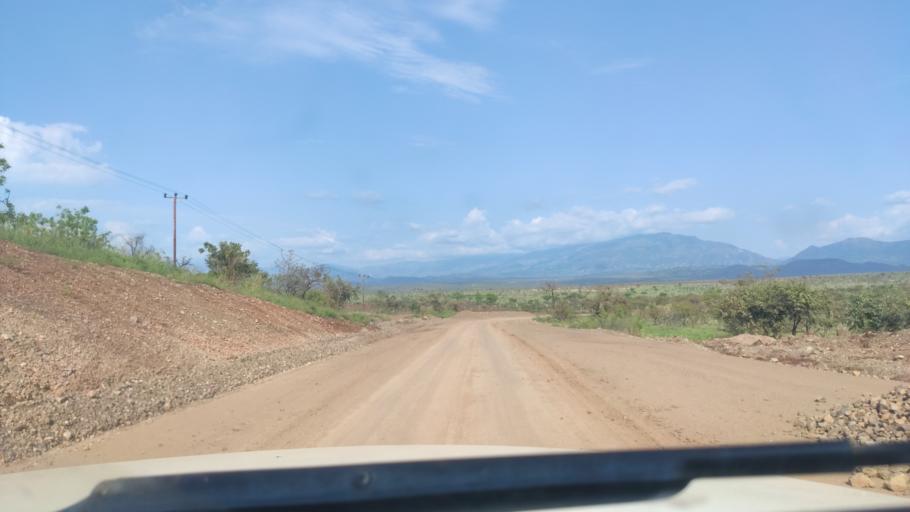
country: ET
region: Southern Nations, Nationalities, and People's Region
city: Felege Neway
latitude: 6.4261
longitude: 37.2251
